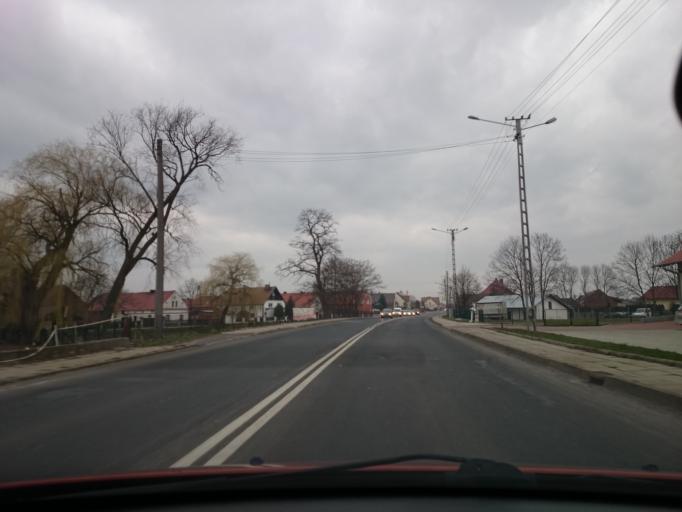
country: PL
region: Opole Voivodeship
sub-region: Powiat opolski
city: Chroscina
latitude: 50.6835
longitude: 17.8284
